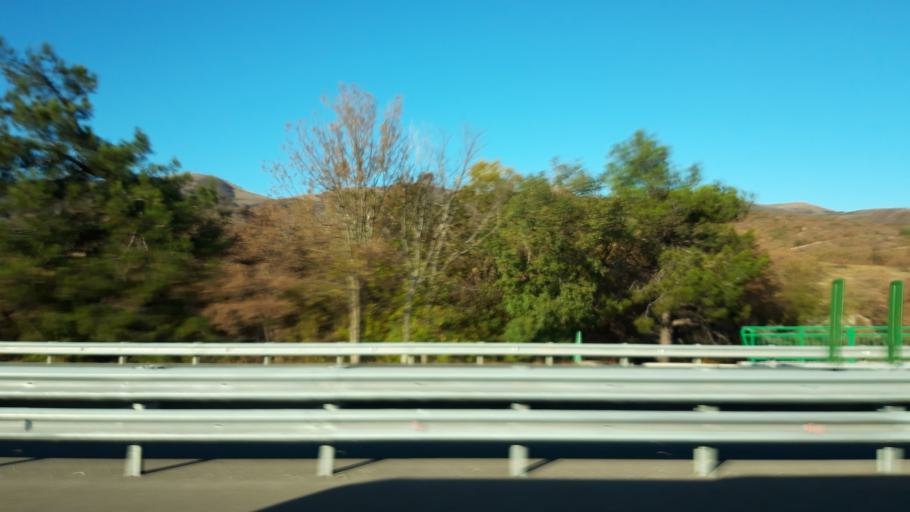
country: RU
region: Krasnodarskiy
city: Kabardinka
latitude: 44.6438
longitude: 37.9691
